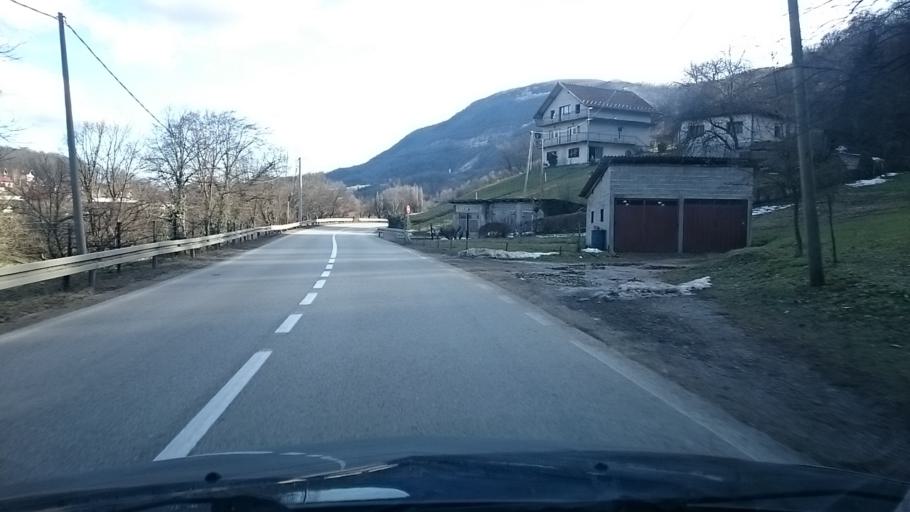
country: BA
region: Republika Srpska
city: Hiseti
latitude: 44.7143
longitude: 17.1647
